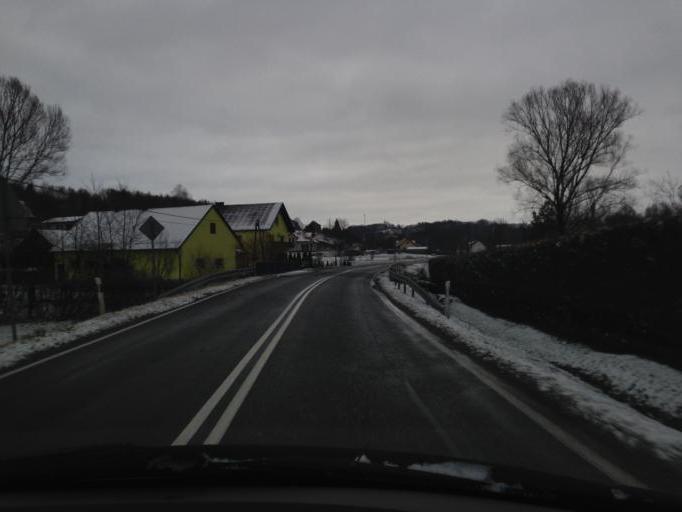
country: PL
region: Lesser Poland Voivodeship
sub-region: Powiat tarnowski
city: Rzepiennik Strzyzewski
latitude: 49.8098
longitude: 21.0201
